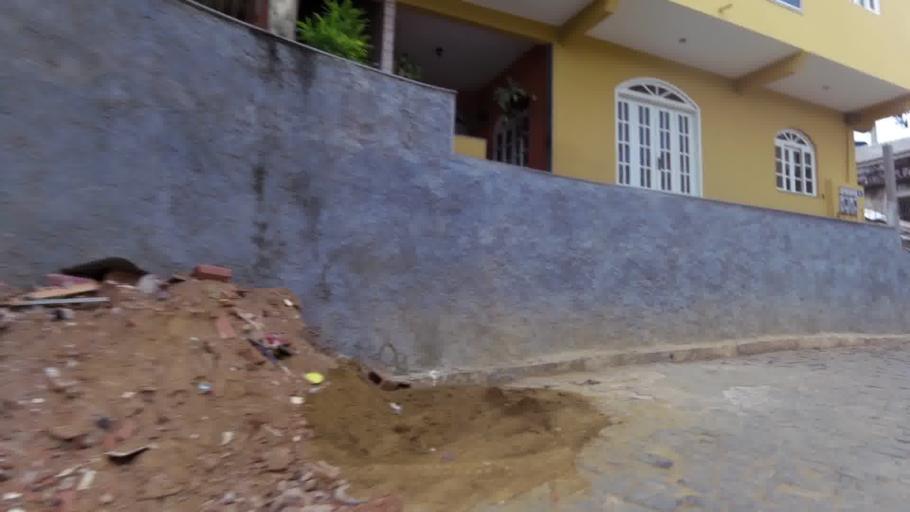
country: BR
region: Espirito Santo
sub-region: Alfredo Chaves
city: Alfredo Chaves
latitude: -20.6381
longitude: -40.7502
